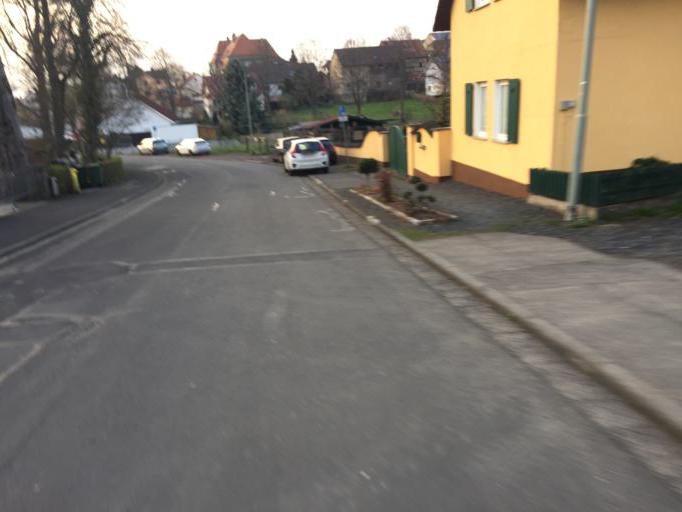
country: DE
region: Hesse
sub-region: Regierungsbezirk Giessen
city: Laubach
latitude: 50.5386
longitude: 8.9920
